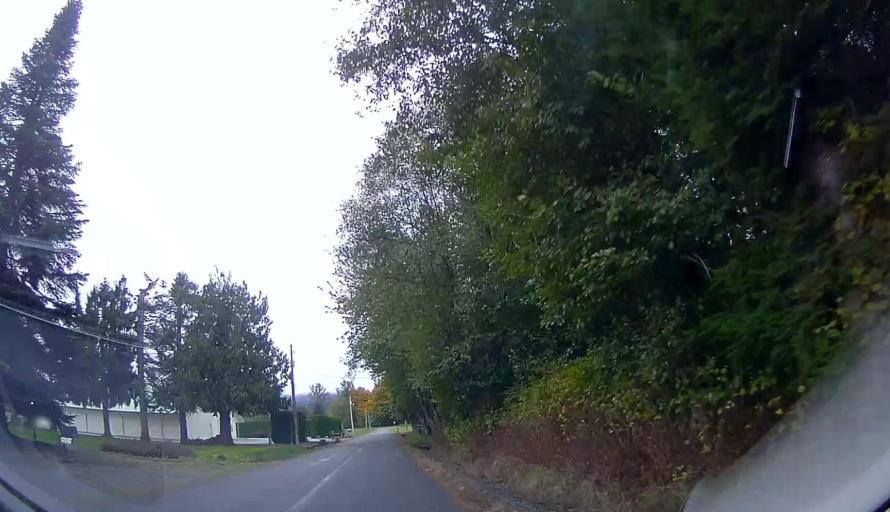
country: US
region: Washington
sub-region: Skagit County
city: Sedro-Woolley
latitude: 48.5097
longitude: -122.1722
